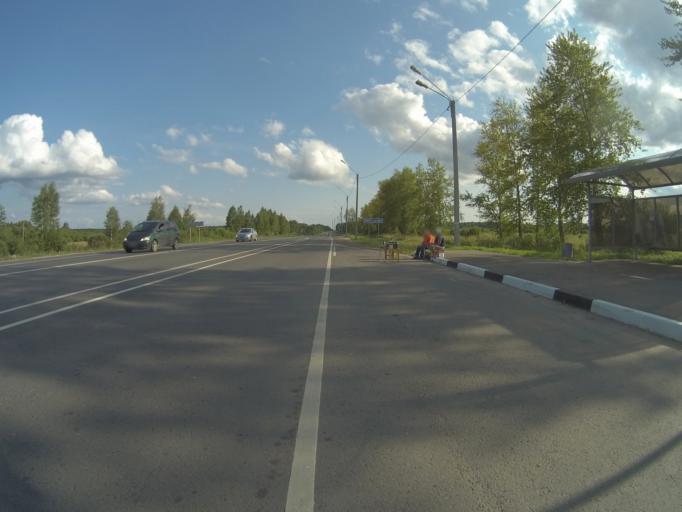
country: RU
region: Vladimir
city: Kideksha
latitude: 56.5899
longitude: 40.5552
